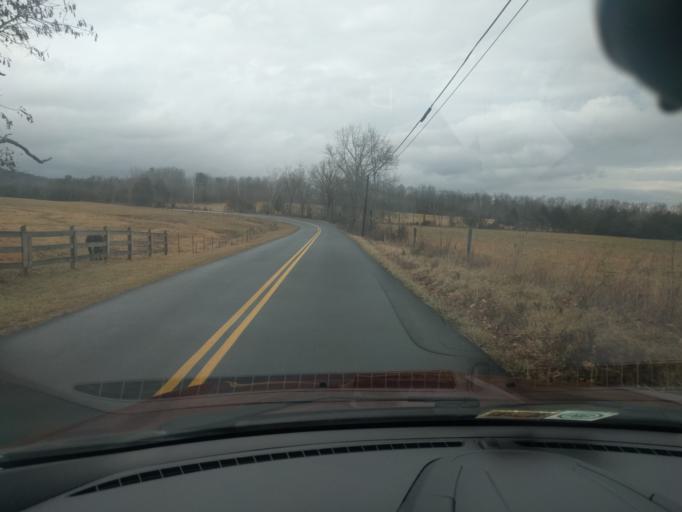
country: US
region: Virginia
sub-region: Botetourt County
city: Fincastle
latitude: 37.5410
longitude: -79.8748
